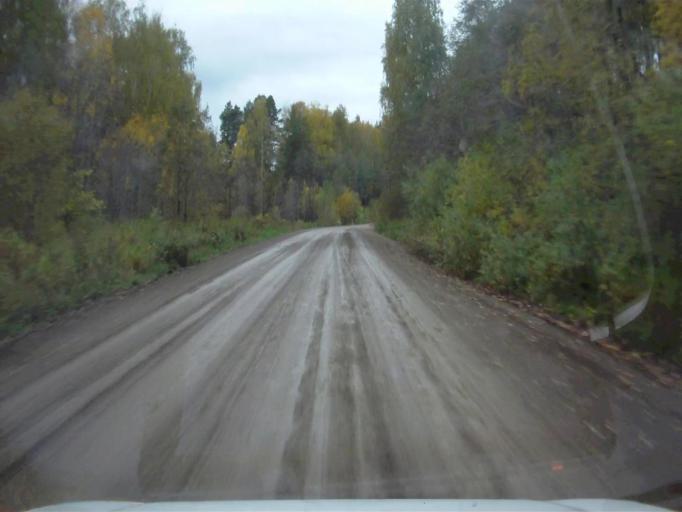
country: RU
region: Chelyabinsk
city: Nyazepetrovsk
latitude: 56.1008
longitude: 59.3894
